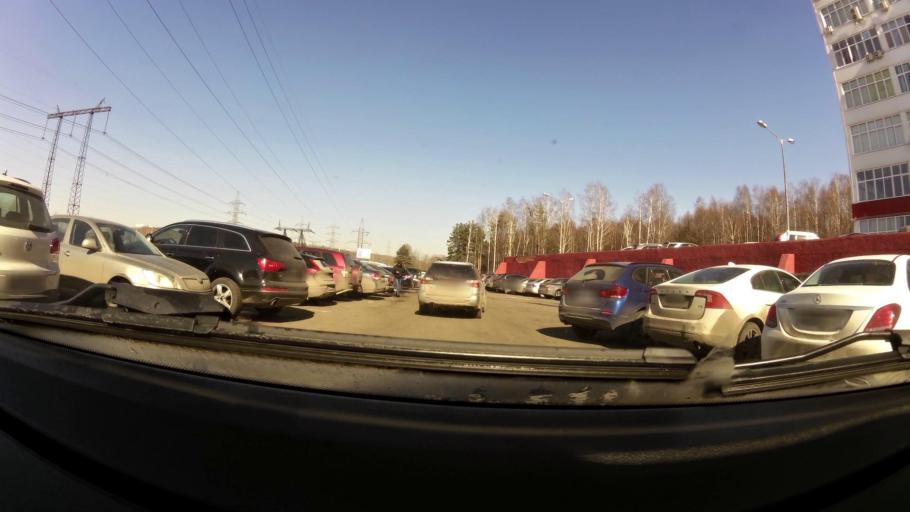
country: RU
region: Moskovskaya
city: Vostryakovo
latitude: 55.6375
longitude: 37.4336
